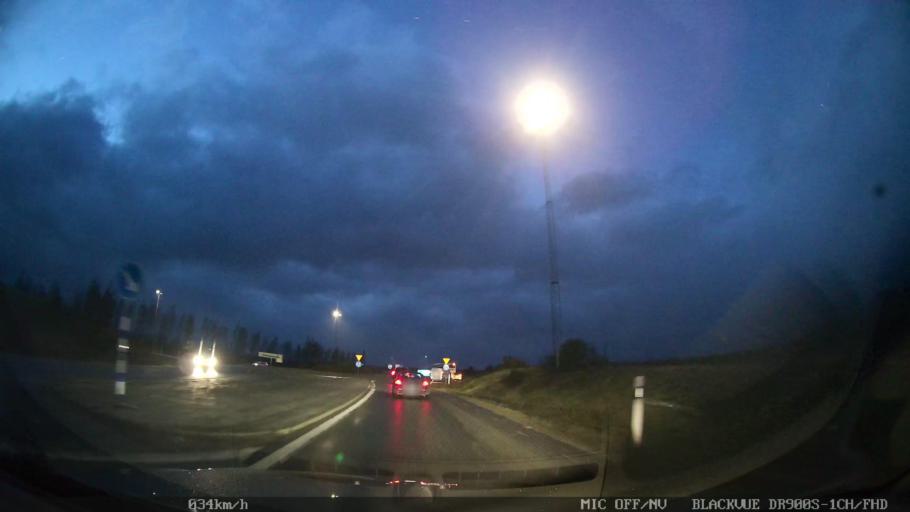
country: SE
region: Skane
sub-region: Hassleholms Kommun
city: Hassleholm
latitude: 56.1788
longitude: 13.7558
